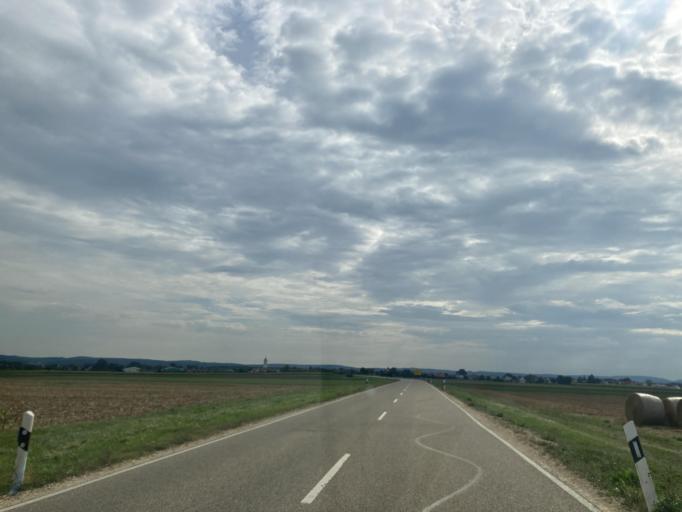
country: DE
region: Bavaria
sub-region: Swabia
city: Munningen
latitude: 48.9202
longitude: 10.5871
